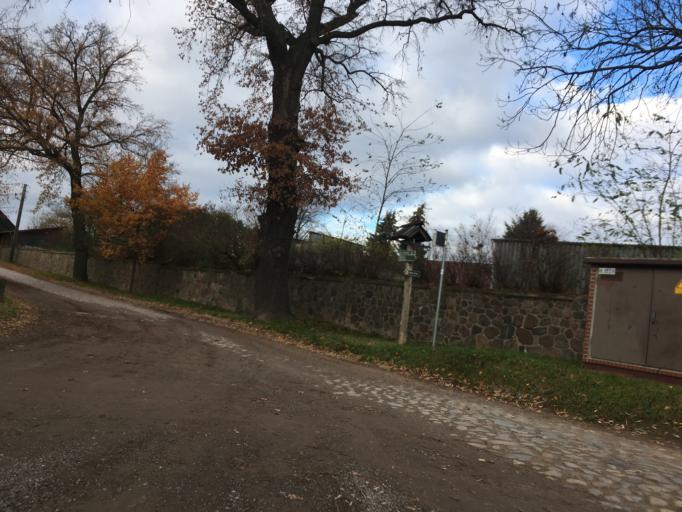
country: DE
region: Brandenburg
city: Muncheberg
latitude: 52.5408
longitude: 14.1769
